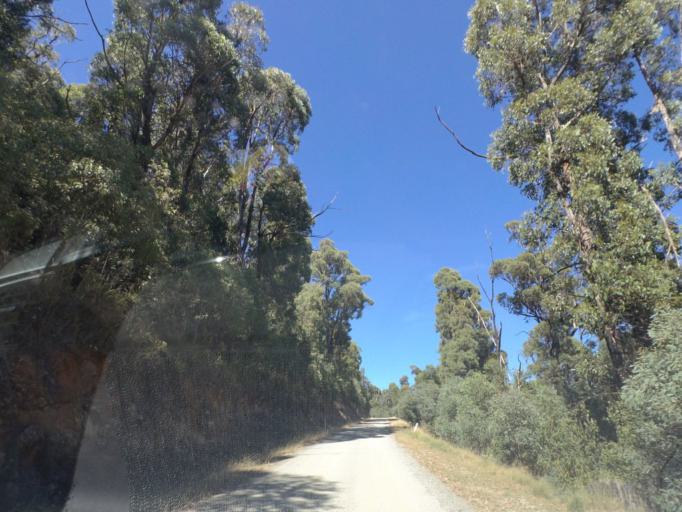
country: AU
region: Victoria
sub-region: Yarra Ranges
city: Millgrove
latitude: -37.5404
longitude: 145.7487
